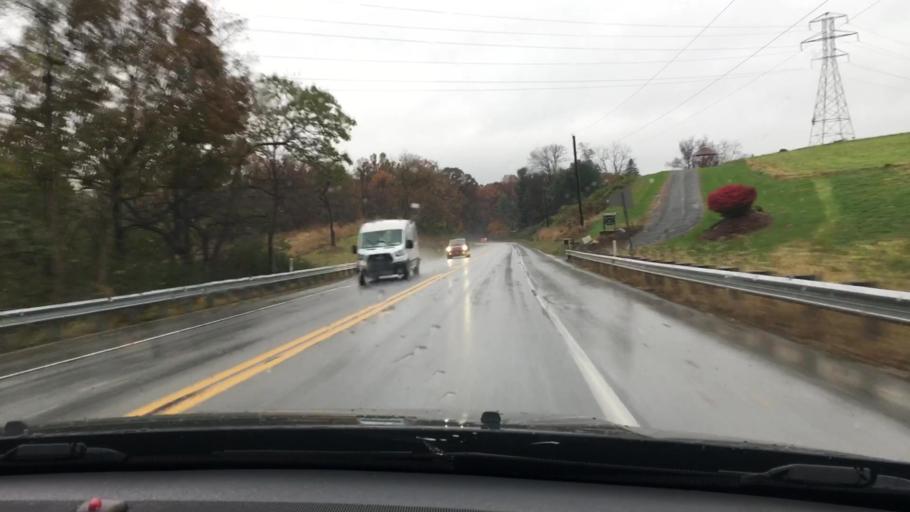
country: US
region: Pennsylvania
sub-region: York County
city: Susquehanna Trails
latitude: 39.8377
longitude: -76.3079
